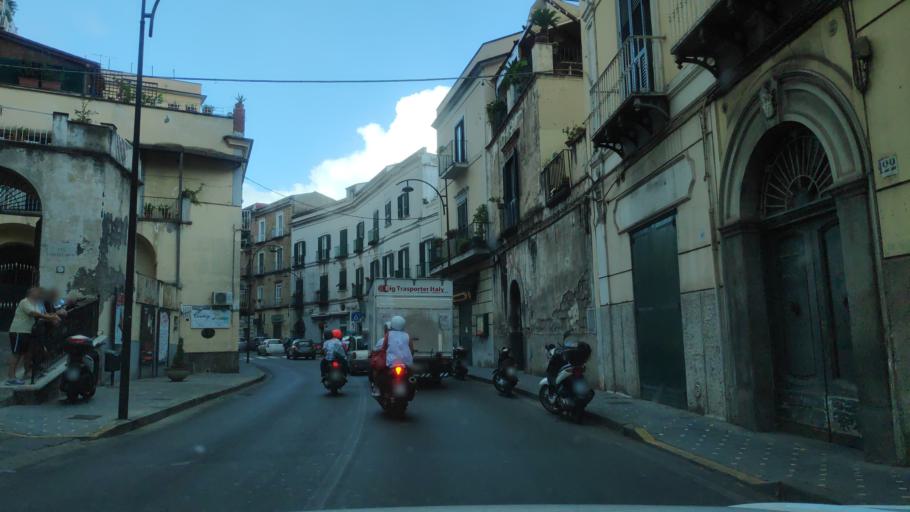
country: IT
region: Campania
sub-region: Provincia di Napoli
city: Meta
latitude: 40.6387
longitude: 14.4187
